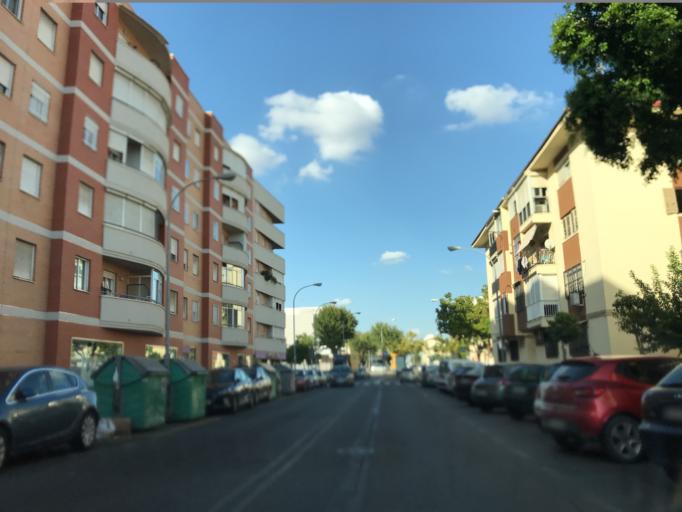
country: ES
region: Andalusia
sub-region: Provincia de Sevilla
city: Sevilla
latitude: 37.4078
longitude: -5.9284
